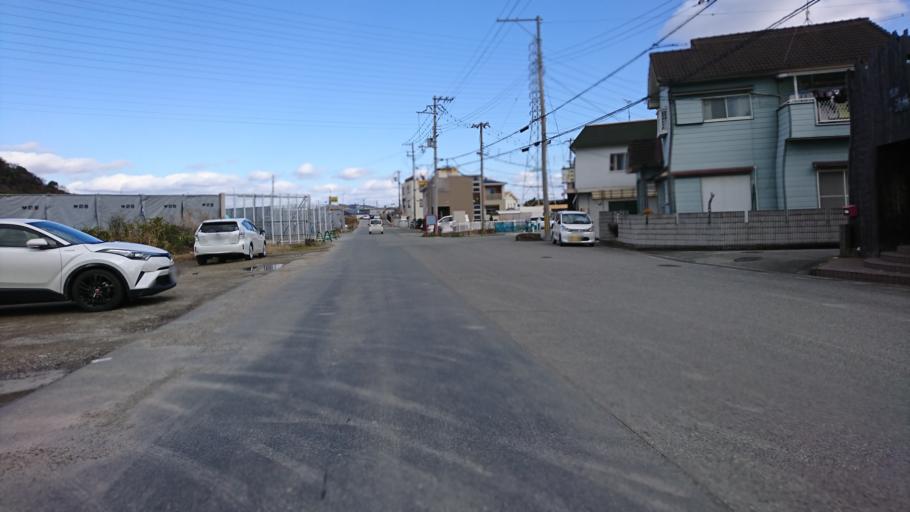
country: JP
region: Hyogo
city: Kakogawacho-honmachi
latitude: 34.7721
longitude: 134.7964
